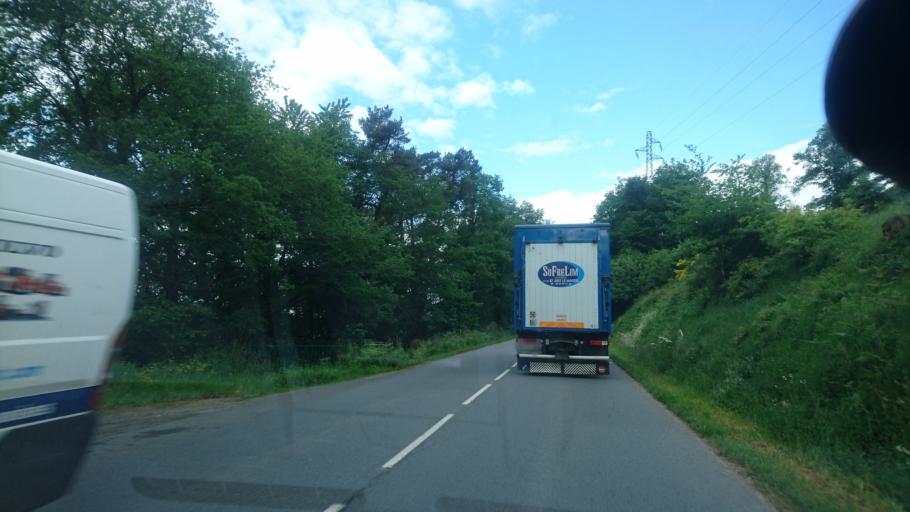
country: FR
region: Limousin
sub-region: Departement de la Haute-Vienne
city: Chateauneuf-la-Foret
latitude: 45.7183
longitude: 1.6092
